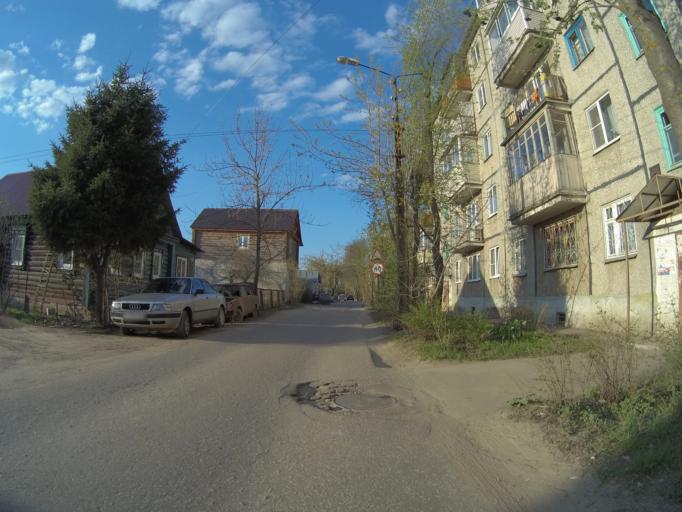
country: RU
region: Vladimir
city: Vladimir
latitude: 56.1433
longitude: 40.3647
